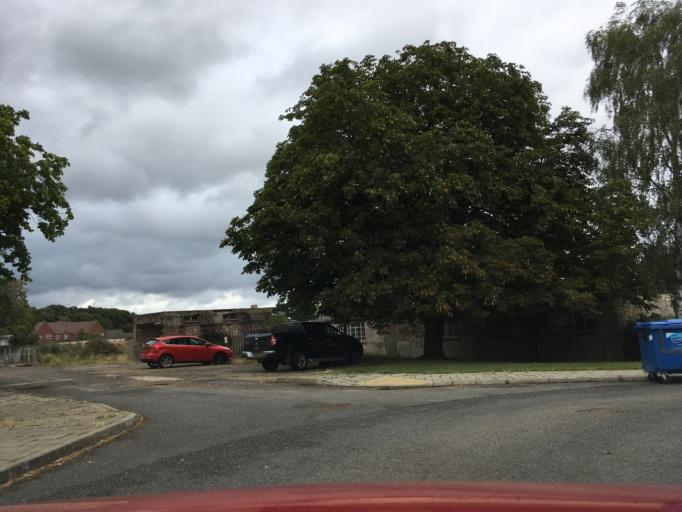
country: GB
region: England
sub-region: Buckinghamshire
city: Bletchley
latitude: 51.9983
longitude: -0.7422
